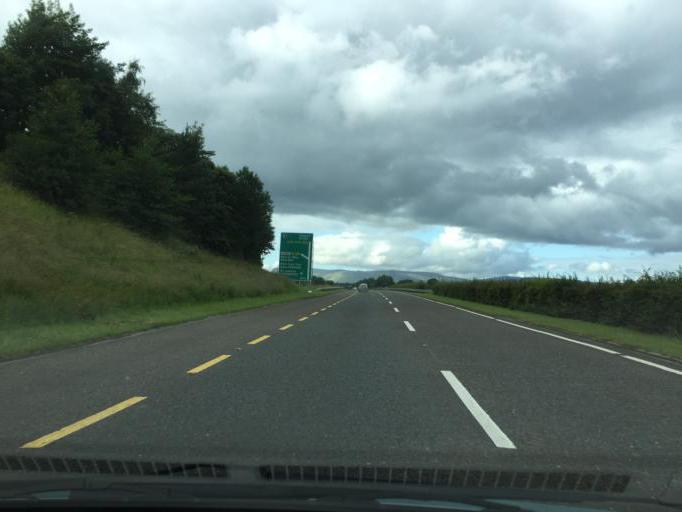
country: IE
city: Ballisodare
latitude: 54.2119
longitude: -8.5017
